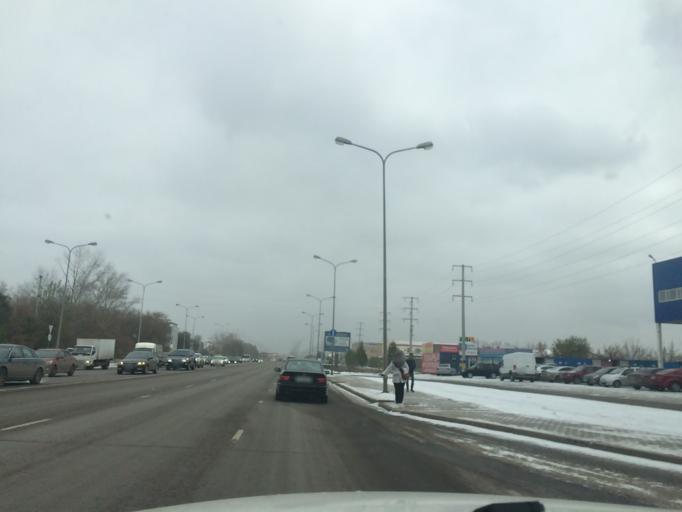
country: KZ
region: Astana Qalasy
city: Astana
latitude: 51.1824
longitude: 71.4571
